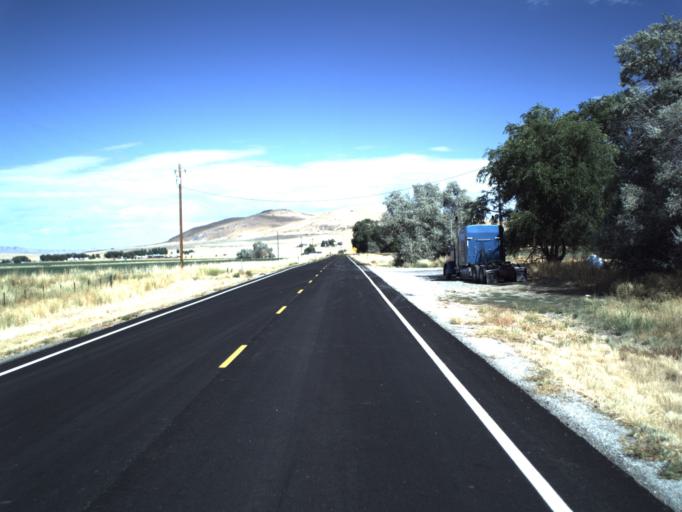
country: US
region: Utah
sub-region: Box Elder County
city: Garland
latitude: 41.7766
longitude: -112.4352
